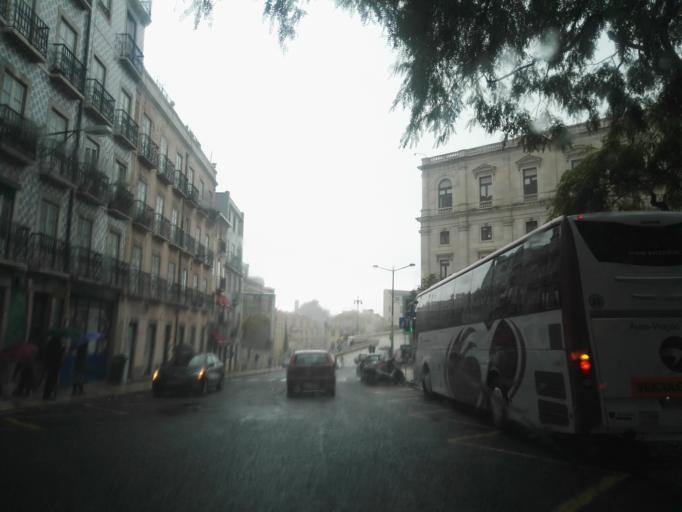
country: PT
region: Lisbon
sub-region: Lisbon
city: Lisbon
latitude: 38.7136
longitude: -9.1533
